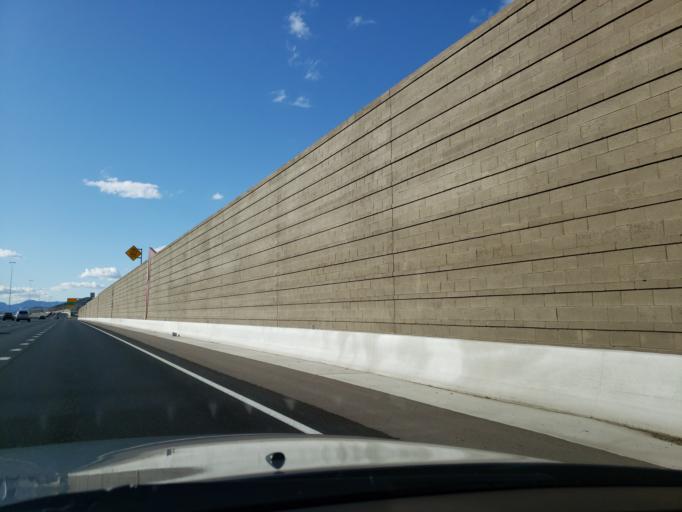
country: US
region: Arizona
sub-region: Maricopa County
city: Guadalupe
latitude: 33.2919
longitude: -112.0233
